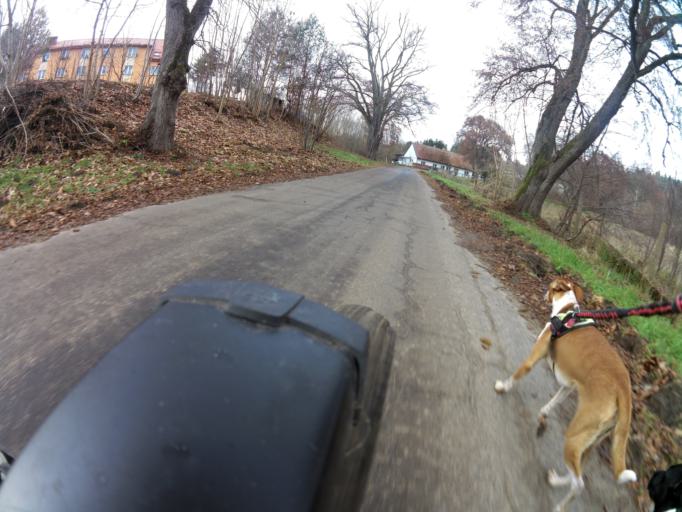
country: PL
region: West Pomeranian Voivodeship
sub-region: Powiat koszalinski
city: Polanow
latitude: 54.0625
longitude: 16.6621
